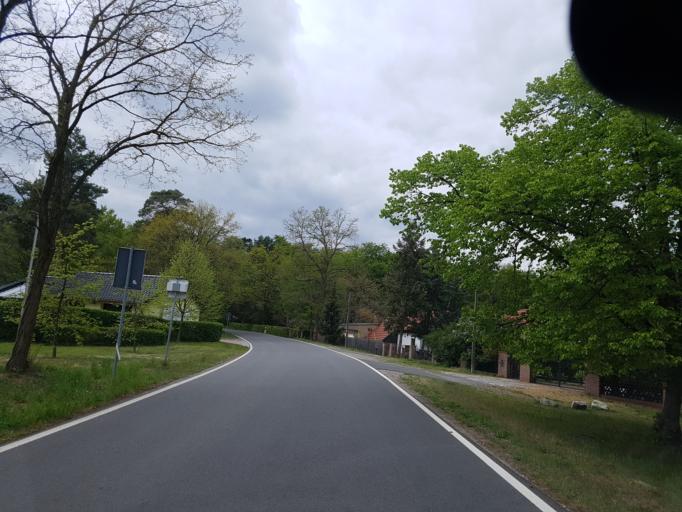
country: DE
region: Brandenburg
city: Altdobern
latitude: 51.6534
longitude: 13.9974
